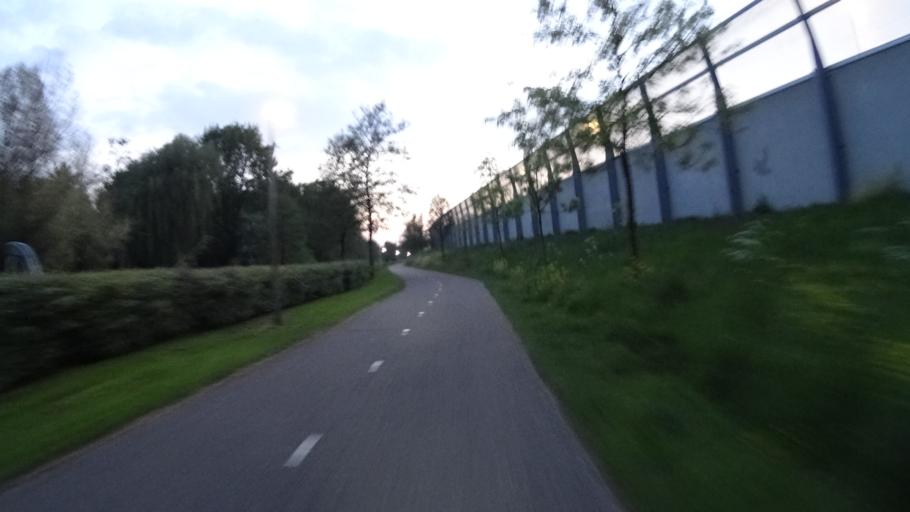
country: NL
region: South Holland
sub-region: Gemeente Sliedrecht
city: Sliedrecht
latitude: 51.8301
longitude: 4.7498
